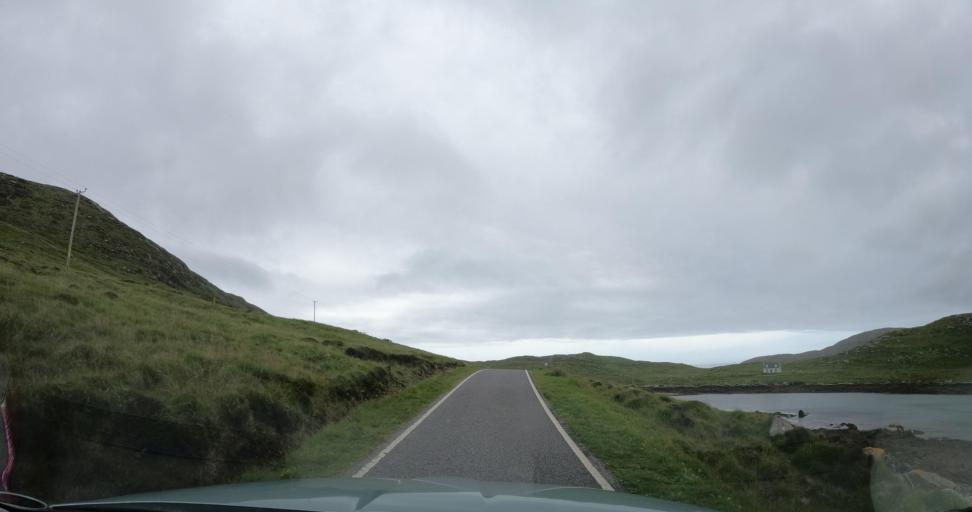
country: GB
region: Scotland
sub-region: Eilean Siar
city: Barra
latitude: 56.9383
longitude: -7.5381
